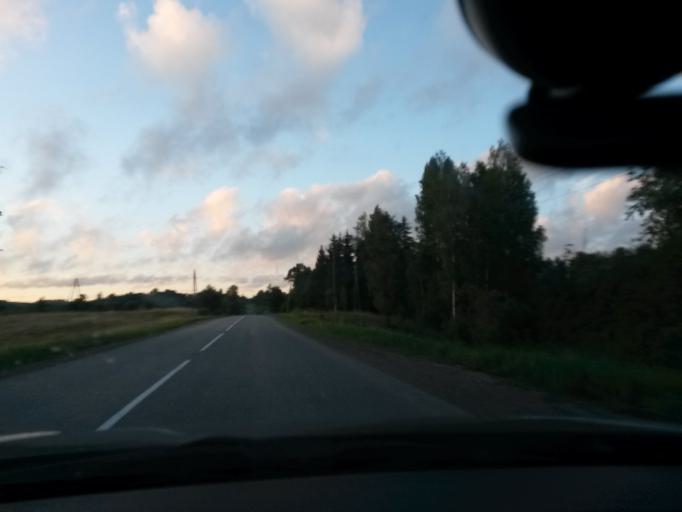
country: LV
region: Madonas Rajons
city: Madona
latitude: 56.7610
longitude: 26.0275
